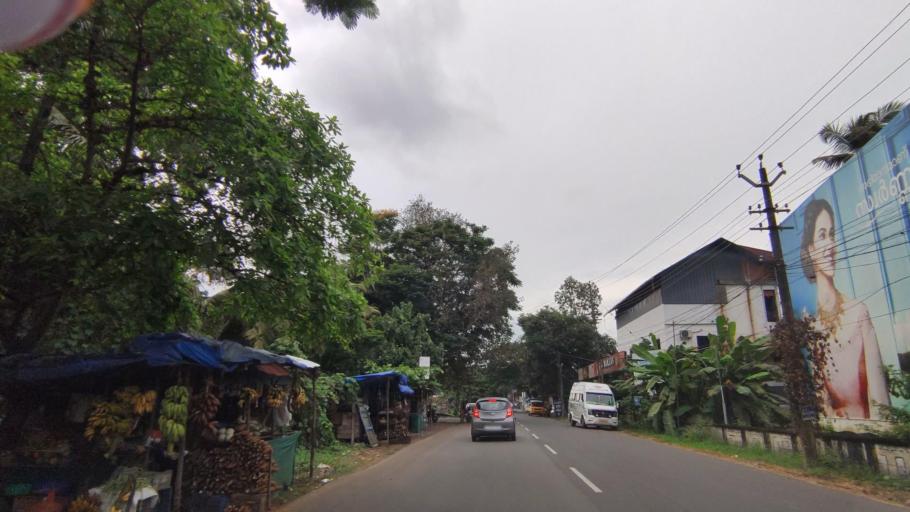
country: IN
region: Kerala
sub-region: Kottayam
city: Kottayam
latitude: 9.6068
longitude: 76.5128
